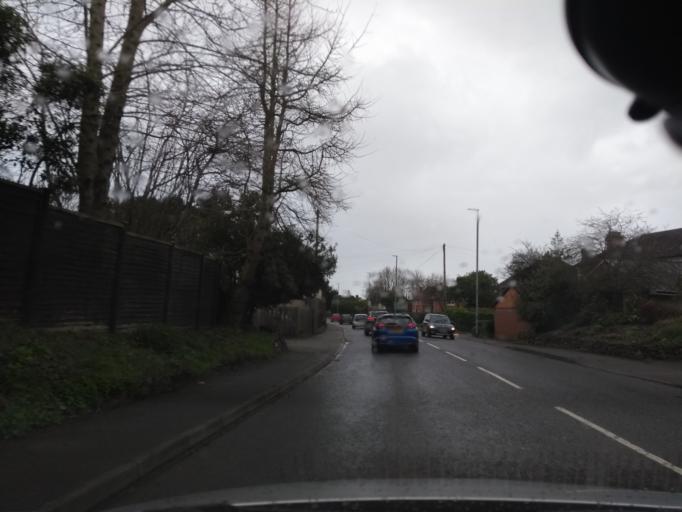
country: GB
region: England
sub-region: Somerset
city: Taunton
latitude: 51.0288
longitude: -3.1243
